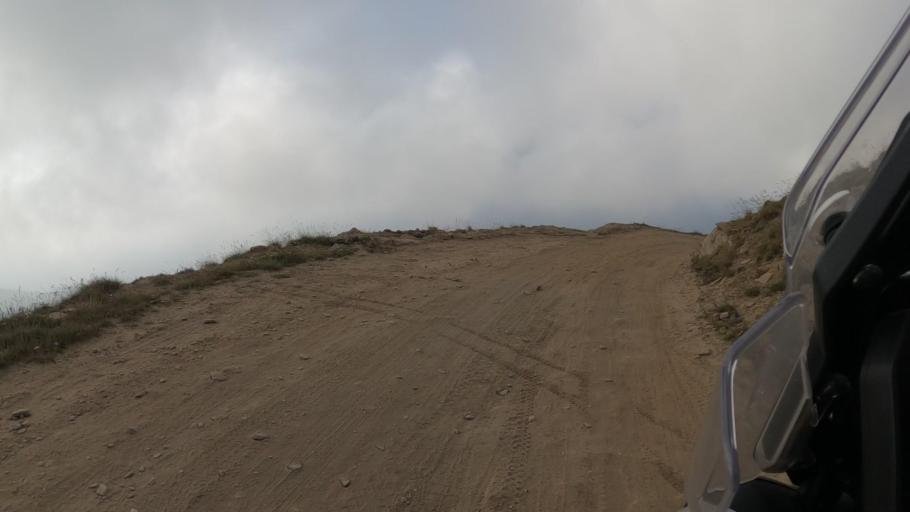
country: IT
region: Piedmont
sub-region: Provincia di Torino
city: Pragelato-Rua
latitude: 45.0441
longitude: 6.9342
